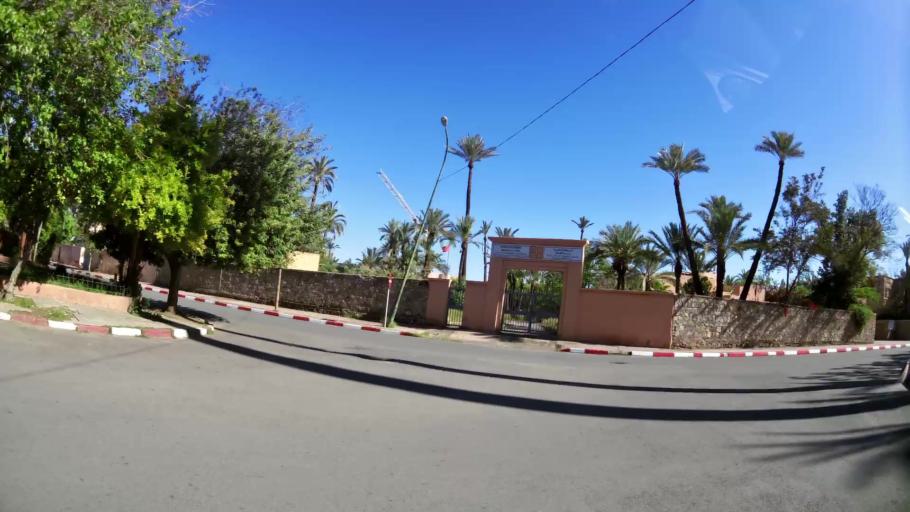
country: MA
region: Marrakech-Tensift-Al Haouz
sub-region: Marrakech
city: Marrakesh
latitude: 31.6399
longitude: -8.0127
